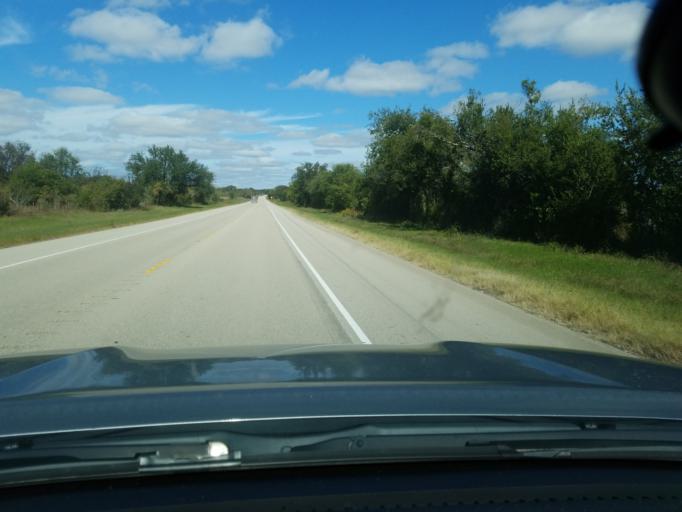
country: US
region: Texas
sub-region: Hamilton County
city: Hamilton
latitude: 31.6021
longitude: -98.1579
